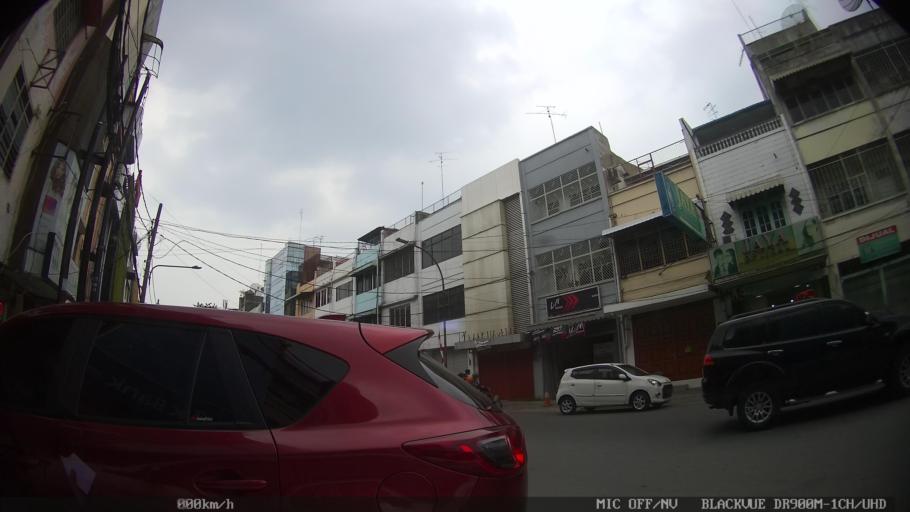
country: ID
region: North Sumatra
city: Medan
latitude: 3.5851
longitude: 98.6924
